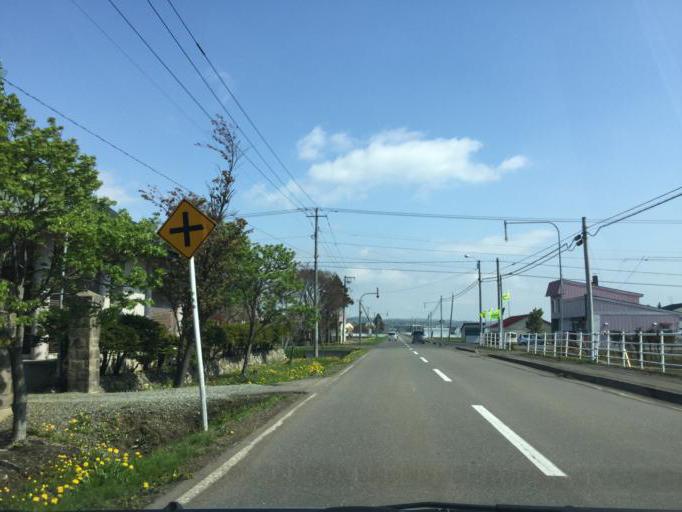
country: JP
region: Hokkaido
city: Iwamizawa
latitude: 43.1390
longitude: 141.7272
